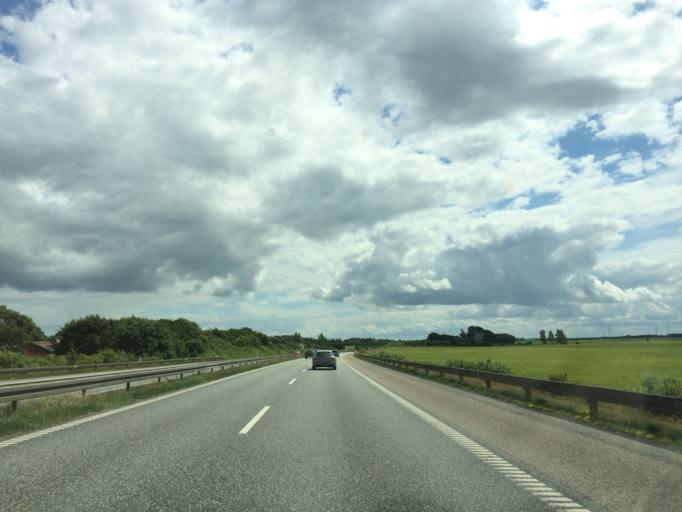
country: DK
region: North Denmark
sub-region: Mariagerfjord Kommune
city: Hobro
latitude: 56.7166
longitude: 9.7240
